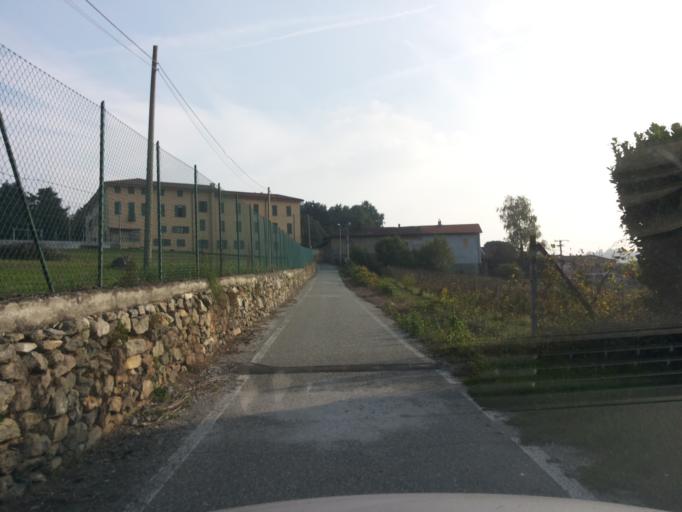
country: IT
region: Piedmont
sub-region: Provincia di Biella
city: Roppolo
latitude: 45.4027
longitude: 8.0584
